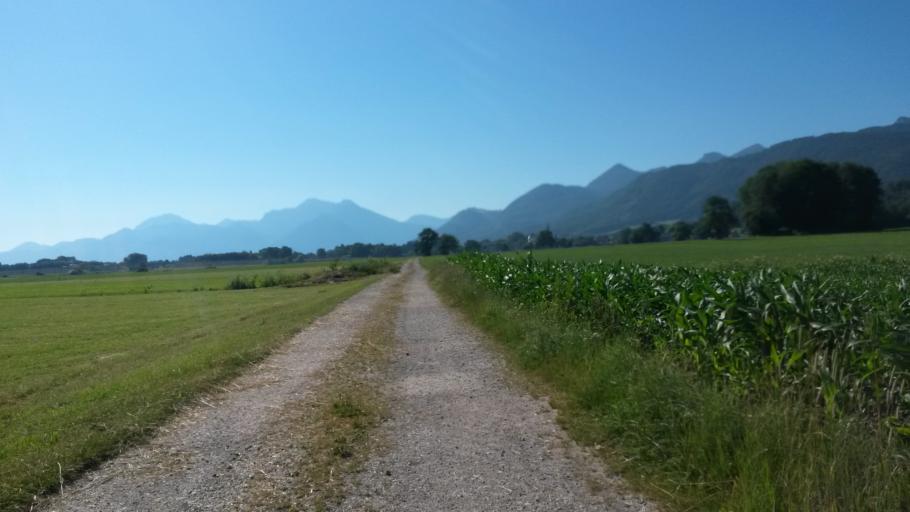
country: DE
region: Bavaria
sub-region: Upper Bavaria
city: Bernau am Chiemsee
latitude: 47.8226
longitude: 12.3626
